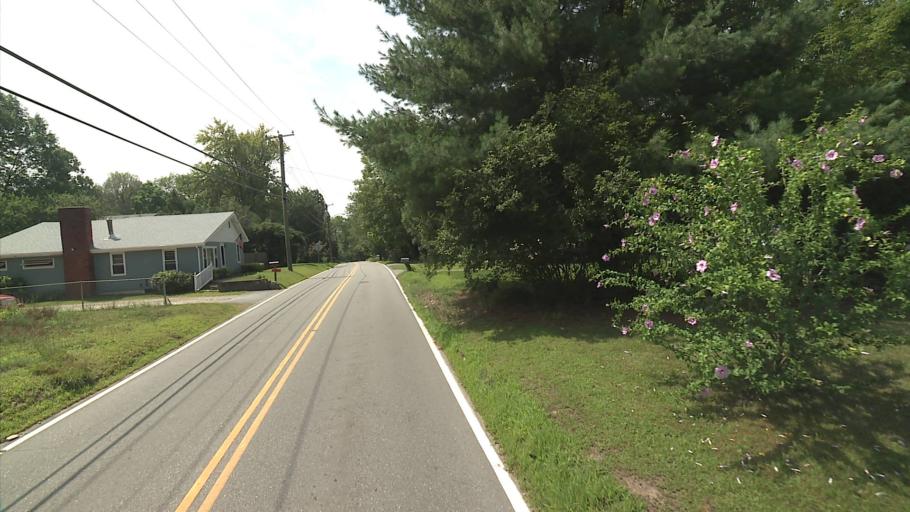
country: US
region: Connecticut
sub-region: Windham County
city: Moosup
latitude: 41.7276
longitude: -71.8672
